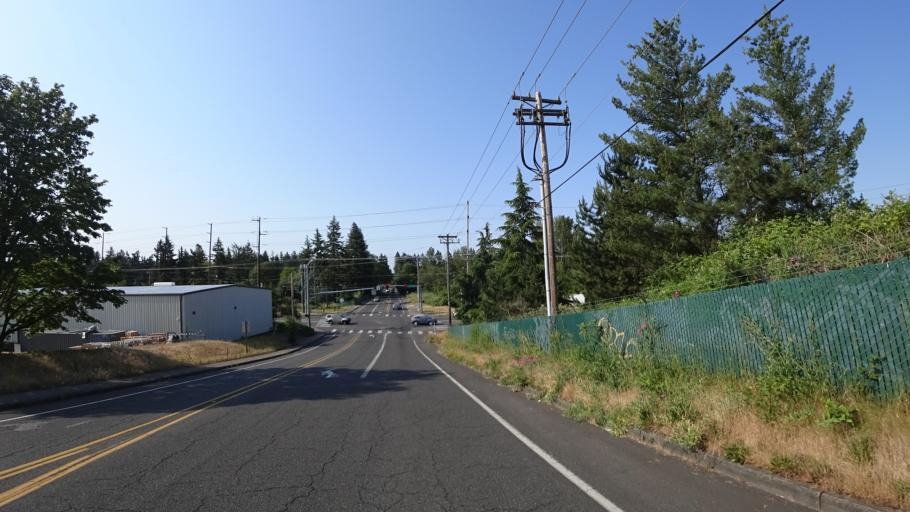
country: US
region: Oregon
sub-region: Multnomah County
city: Lents
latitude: 45.4568
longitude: -122.5991
